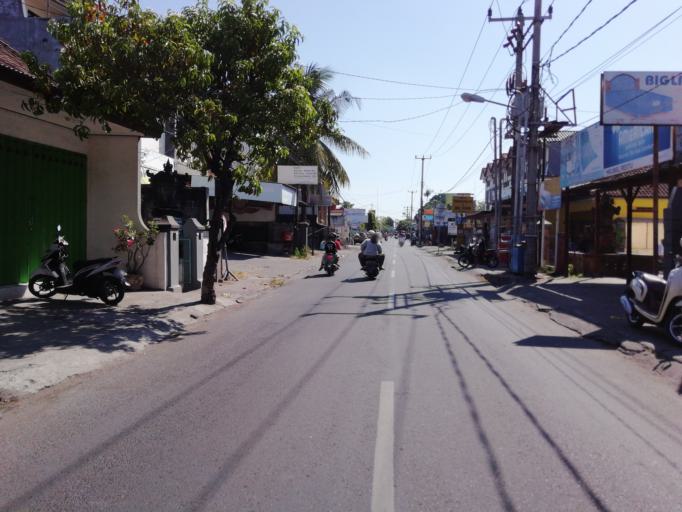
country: ID
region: Bali
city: Karyadharma
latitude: -8.7005
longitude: 115.2224
